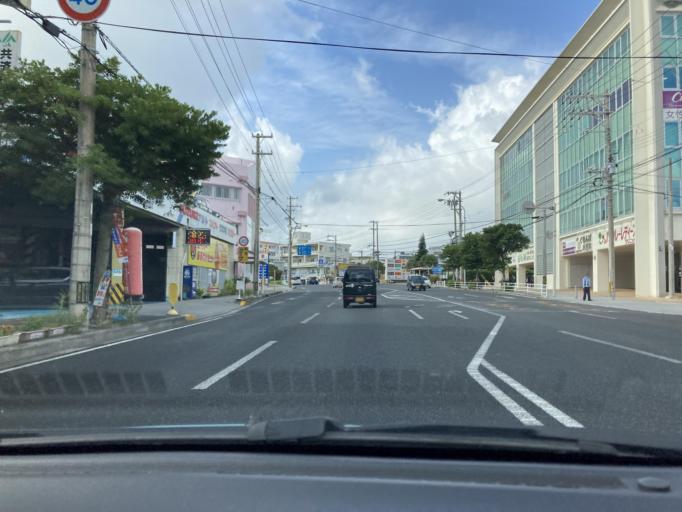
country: JP
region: Okinawa
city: Ginowan
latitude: 26.2531
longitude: 127.7389
